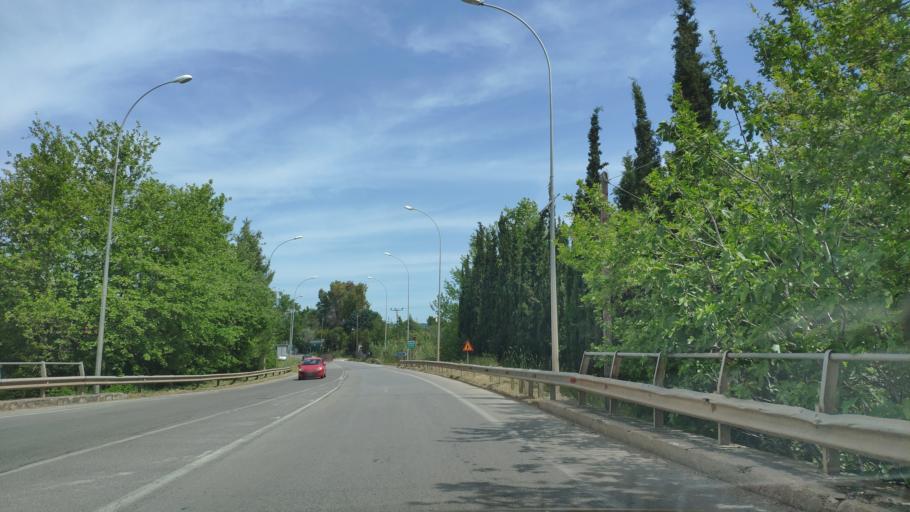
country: GR
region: Attica
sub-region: Nomarchia Anatolikis Attikis
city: Afidnes
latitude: 38.1888
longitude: 23.8545
